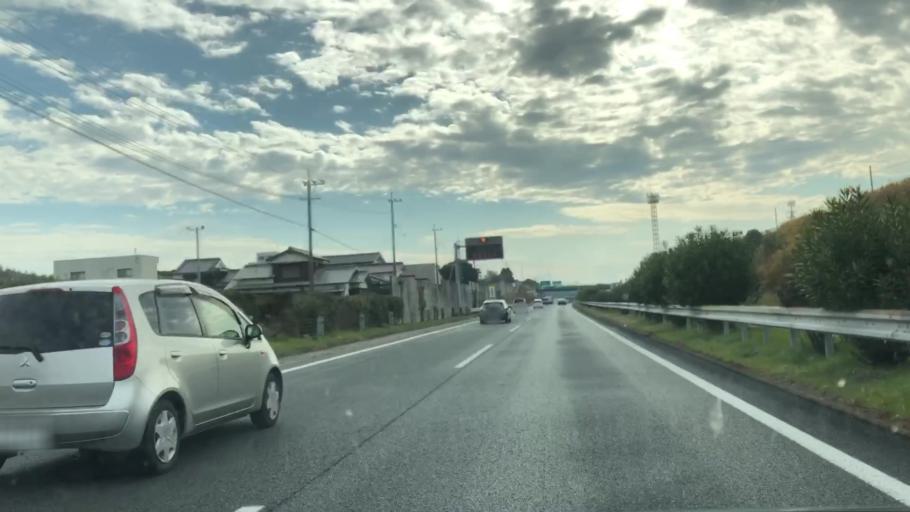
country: JP
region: Fukuoka
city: Kurume
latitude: 33.2606
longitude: 130.5382
